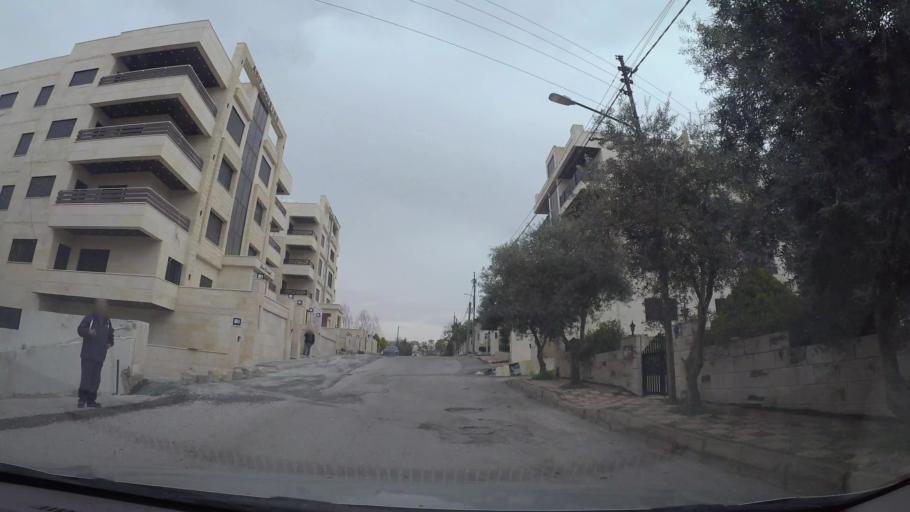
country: JO
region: Amman
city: Umm as Summaq
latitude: 31.8905
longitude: 35.8535
